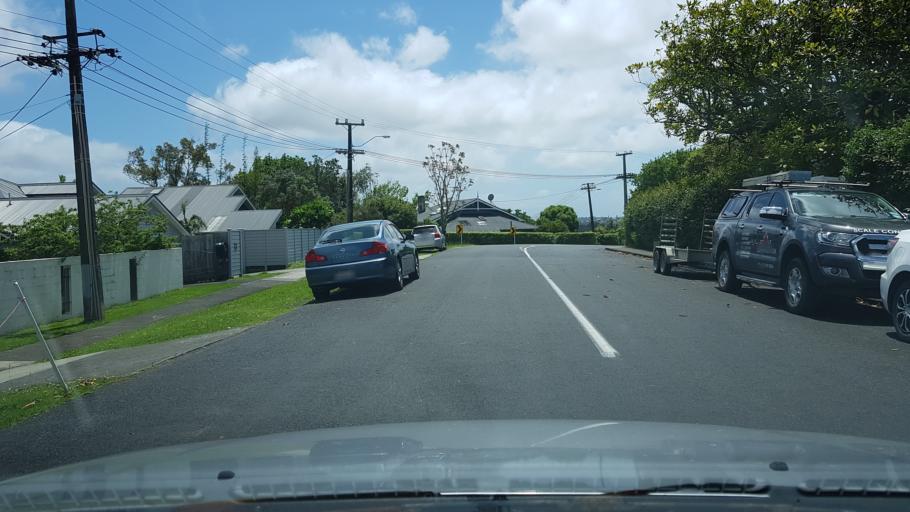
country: NZ
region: Auckland
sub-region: Auckland
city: North Shore
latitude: -36.8085
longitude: 174.7148
